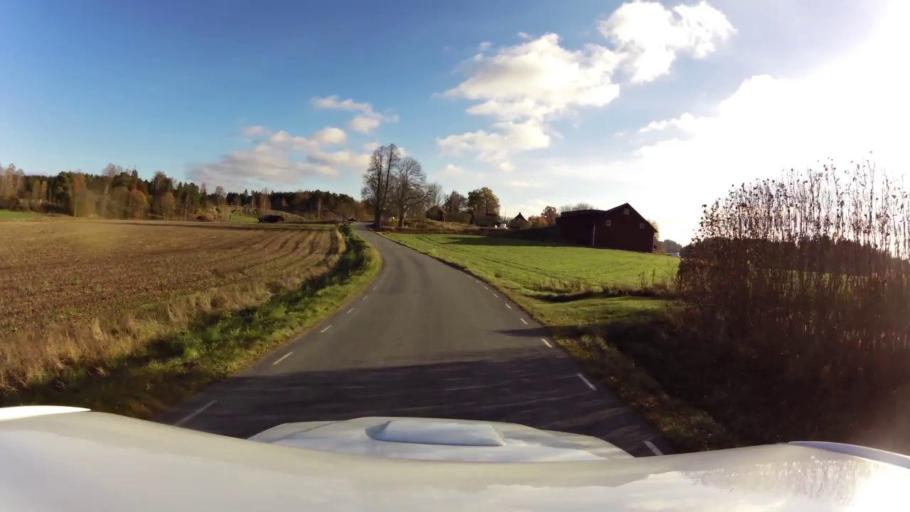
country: SE
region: OEstergoetland
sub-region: Linkopings Kommun
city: Vikingstad
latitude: 58.2572
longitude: 15.4616
